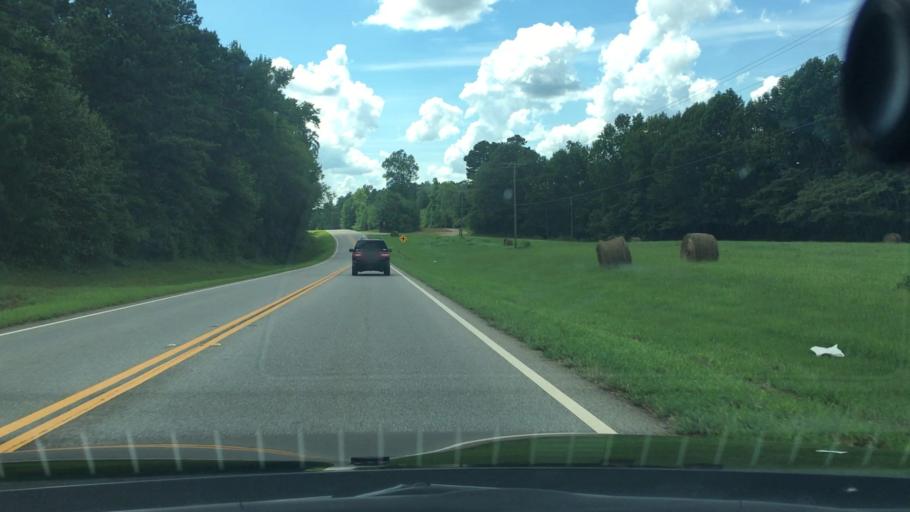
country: US
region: Georgia
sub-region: Putnam County
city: Eatonton
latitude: 33.3121
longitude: -83.4540
